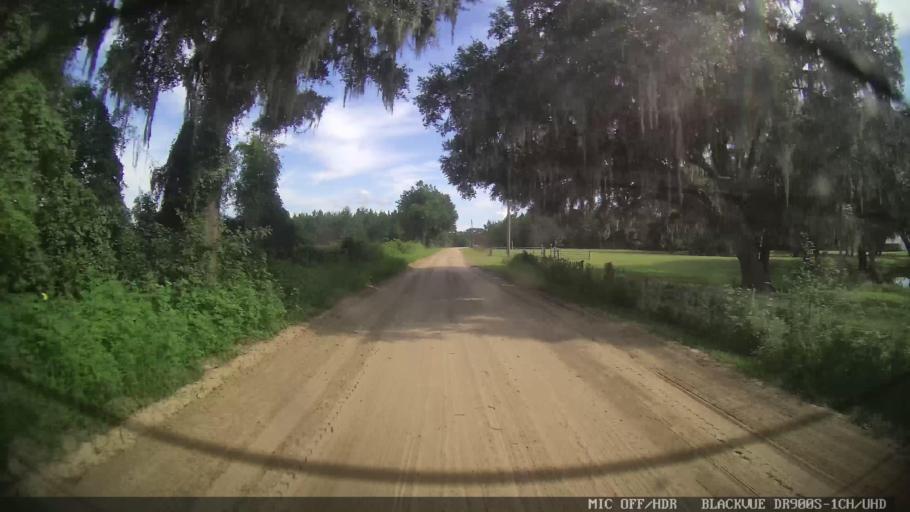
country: US
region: Georgia
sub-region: Echols County
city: Statenville
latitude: 30.6150
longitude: -83.2017
